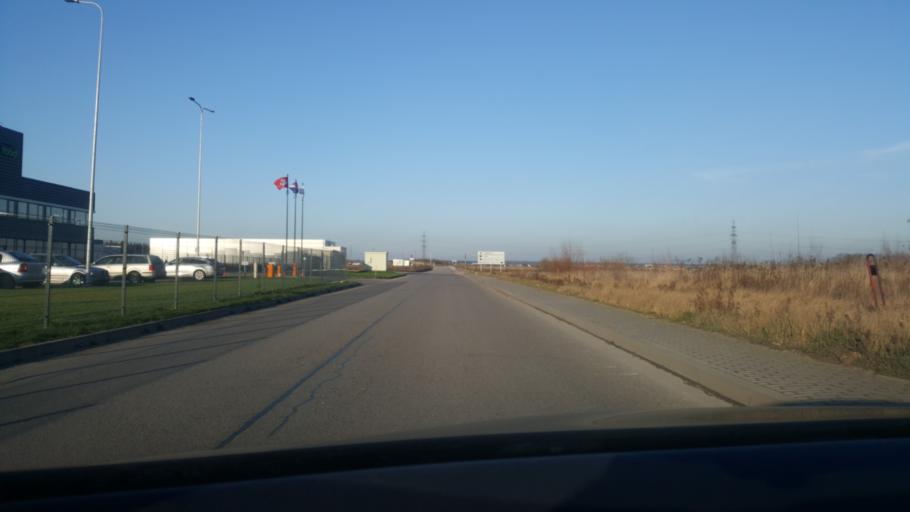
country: LT
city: Ramuciai
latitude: 54.9307
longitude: 24.0370
